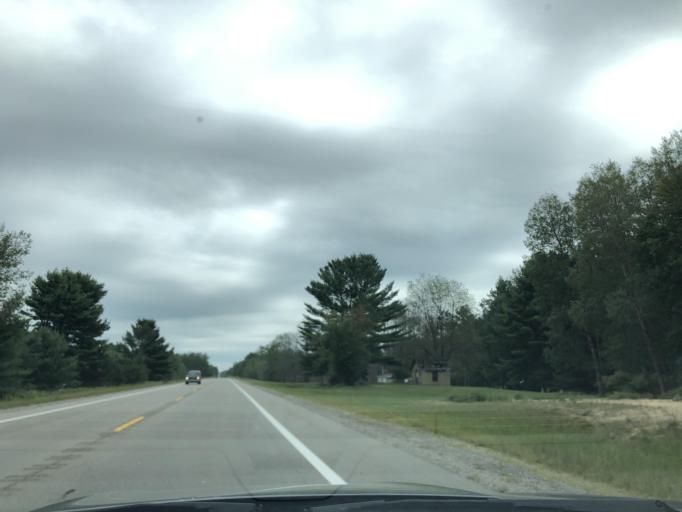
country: US
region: Michigan
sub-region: Clare County
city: Harrison
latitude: 44.0312
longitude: -85.0036
